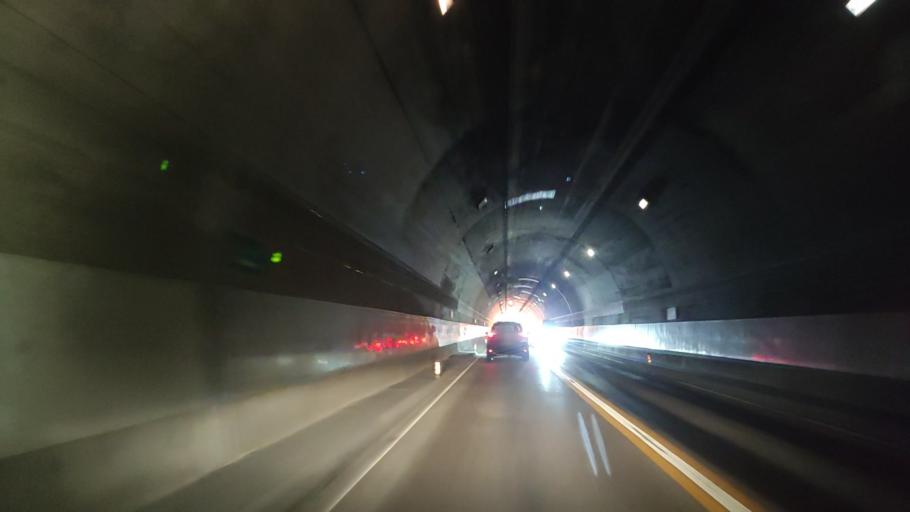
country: JP
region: Tokushima
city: Kamojimacho-jogejima
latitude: 34.1667
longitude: 134.3321
